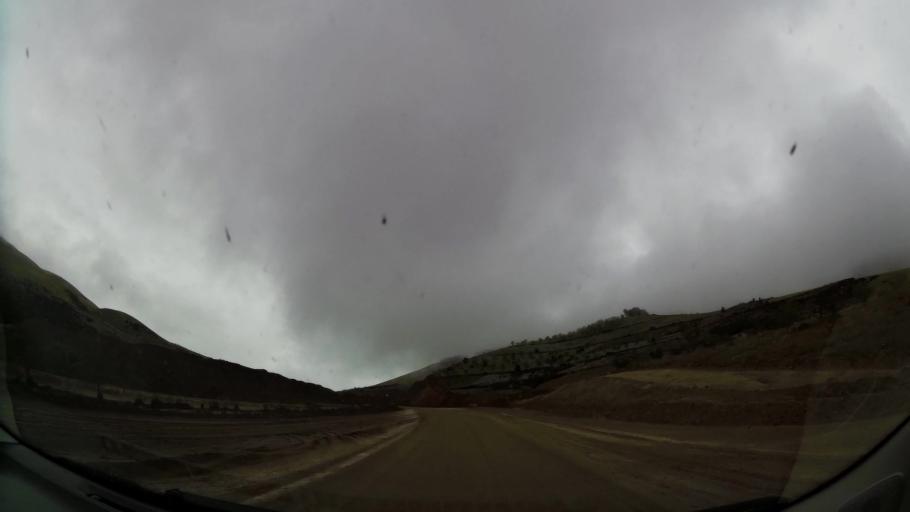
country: MA
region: Taza-Al Hoceima-Taounate
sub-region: Taza
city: Ajdir
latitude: 34.9101
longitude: -3.7964
